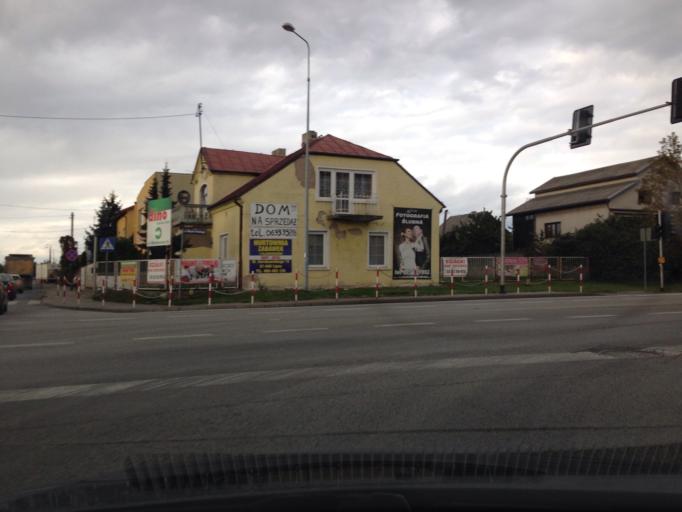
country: PL
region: Kujawsko-Pomorskie
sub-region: Powiat lipnowski
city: Lipno
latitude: 52.8525
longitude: 19.1756
